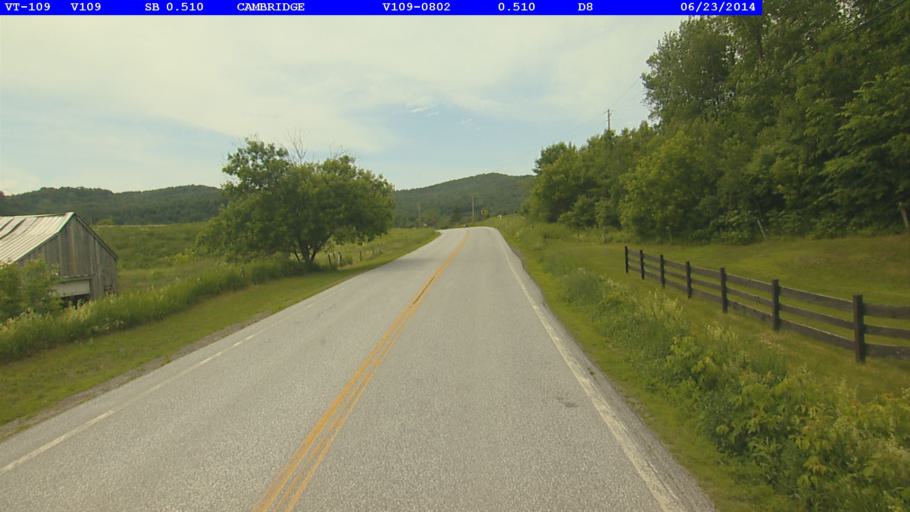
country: US
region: Vermont
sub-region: Lamoille County
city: Johnson
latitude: 44.6538
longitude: -72.8182
